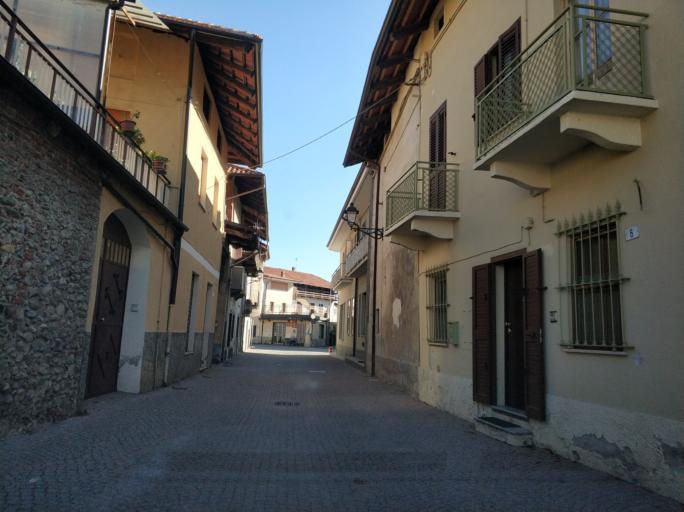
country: IT
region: Piedmont
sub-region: Provincia di Torino
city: Grosso
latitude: 45.2573
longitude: 7.5585
